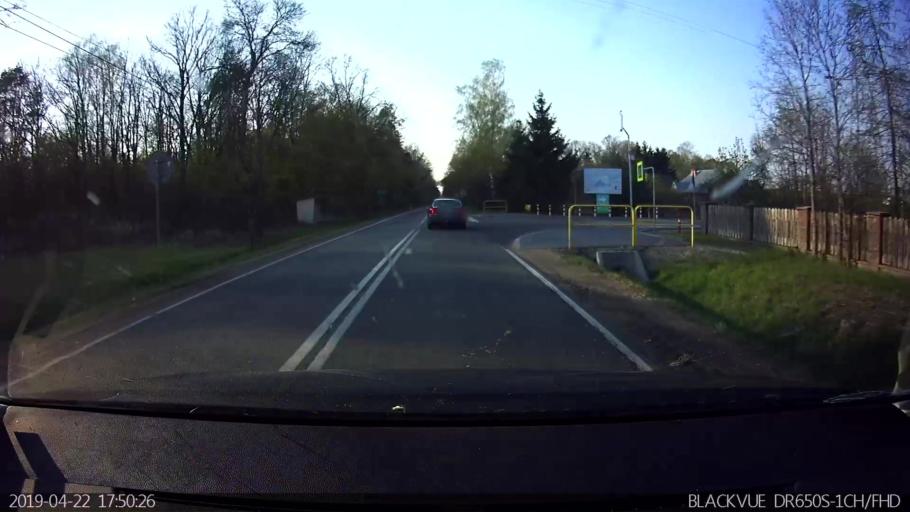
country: PL
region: Masovian Voivodeship
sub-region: Powiat wegrowski
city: Wegrow
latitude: 52.4245
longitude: 22.0019
